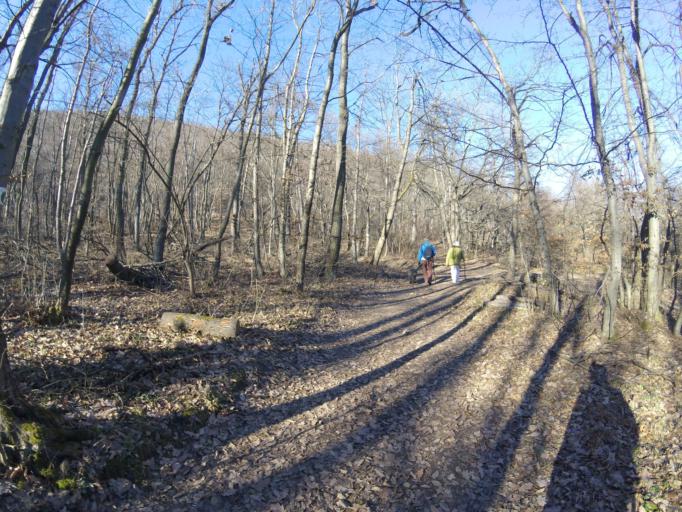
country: HU
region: Pest
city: Pilisszanto
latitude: 47.6851
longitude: 18.8797
